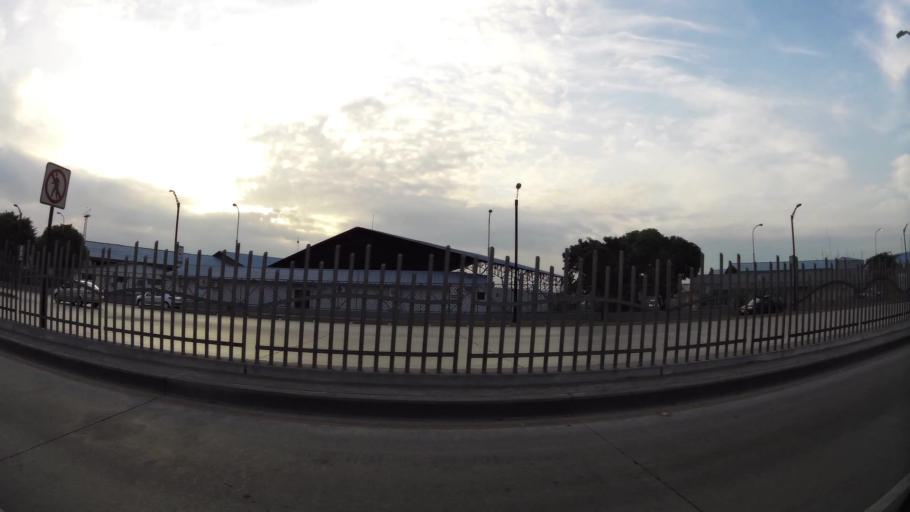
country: EC
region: Guayas
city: Eloy Alfaro
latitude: -2.1662
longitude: -79.8921
